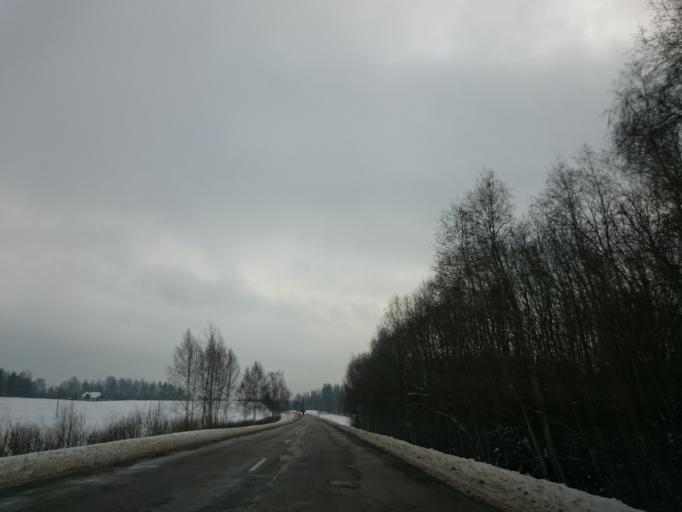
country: LV
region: Pargaujas
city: Stalbe
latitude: 57.3489
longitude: 25.1052
